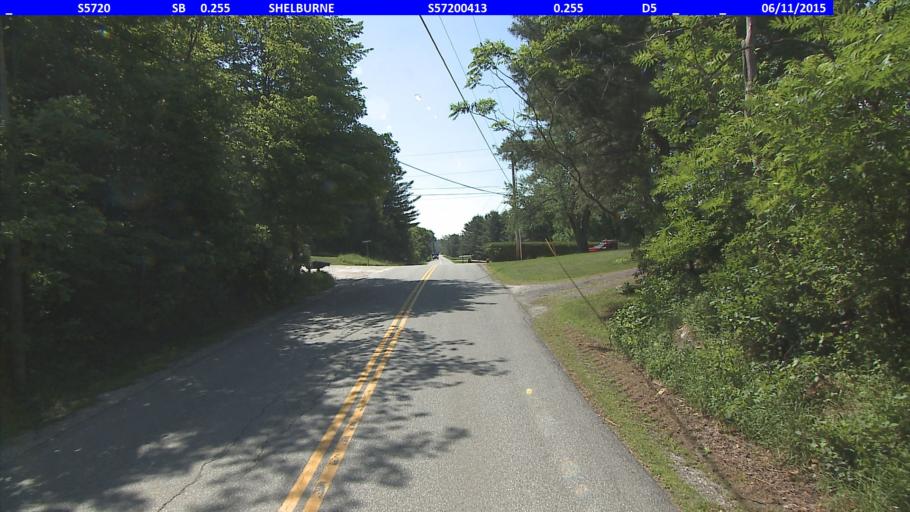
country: US
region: Vermont
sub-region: Chittenden County
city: Hinesburg
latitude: 44.3620
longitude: -73.1984
